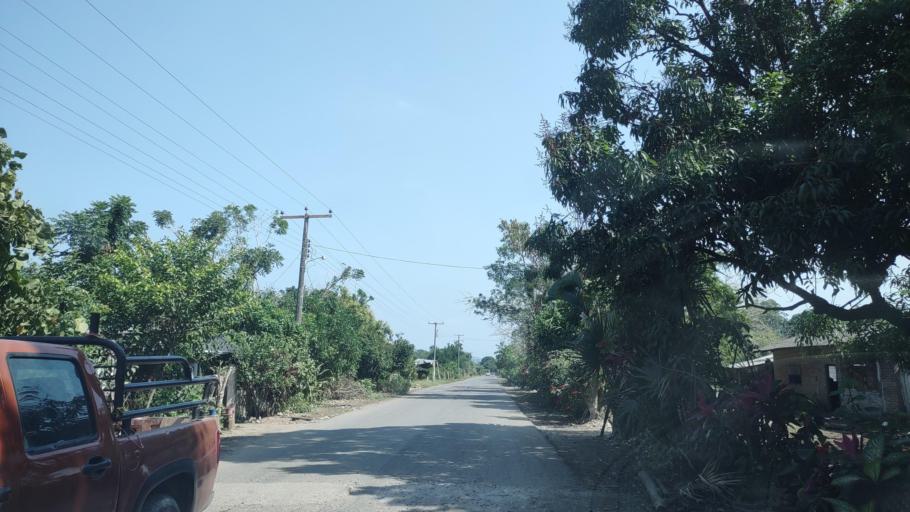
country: MX
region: Puebla
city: Espinal
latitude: 20.2563
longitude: -97.3267
